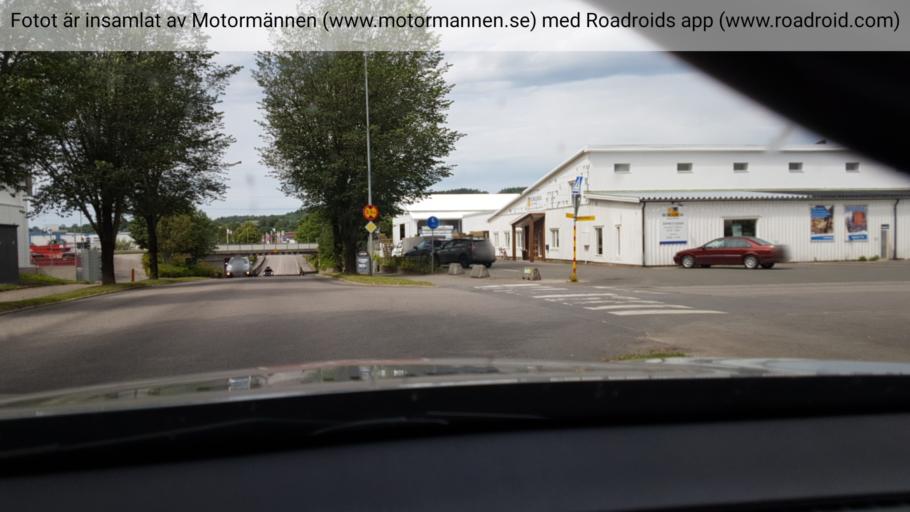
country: SE
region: Vaestra Goetaland
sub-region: Falkopings Kommun
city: Falkoeping
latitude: 58.1659
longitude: 13.5474
